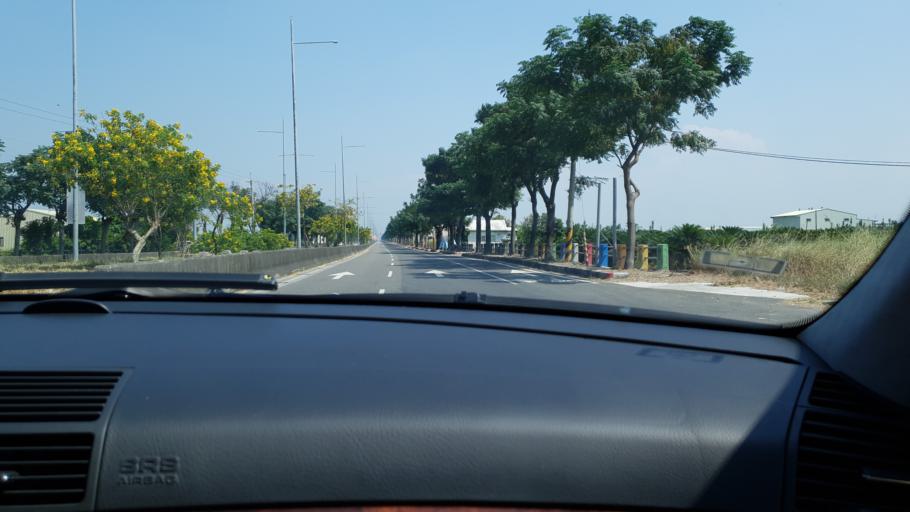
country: TW
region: Taiwan
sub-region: Yunlin
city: Douliu
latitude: 23.7355
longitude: 120.4335
